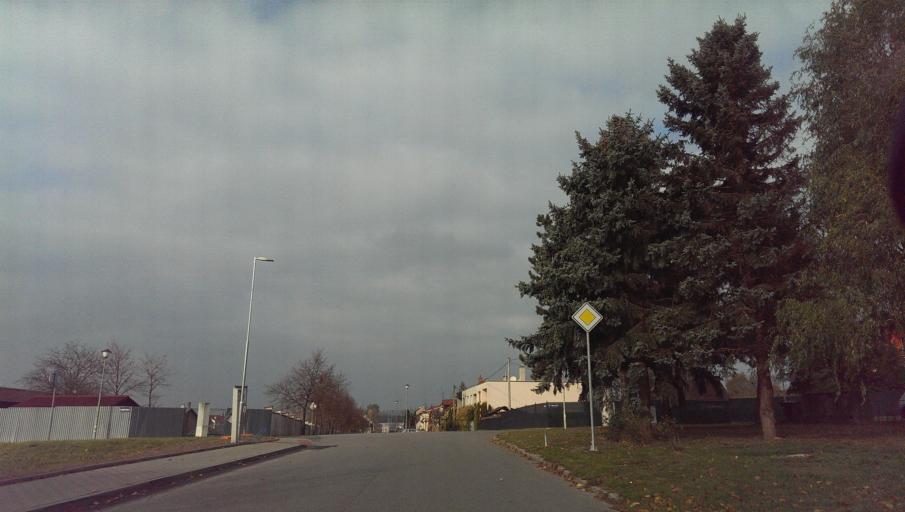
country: CZ
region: Zlin
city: Tlumacov
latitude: 49.2568
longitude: 17.5033
